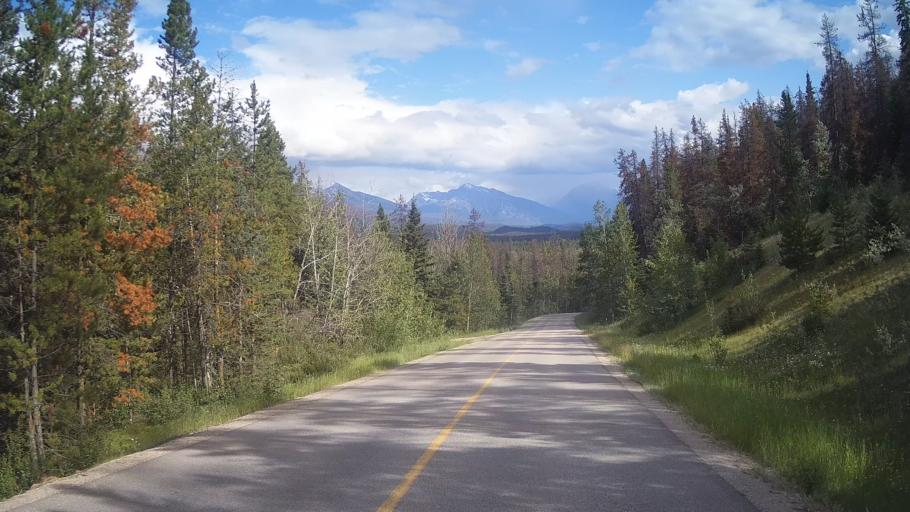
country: CA
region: Alberta
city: Jasper Park Lodge
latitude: 52.8588
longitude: -118.0980
